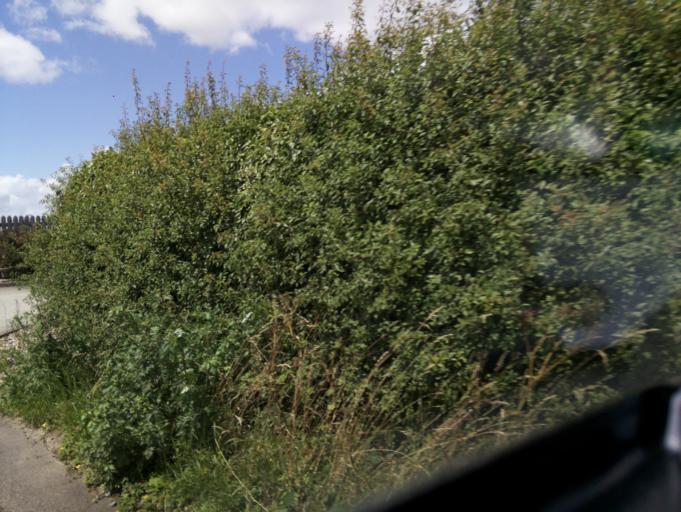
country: GB
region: England
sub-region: Nottinghamshire
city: Burton Joyce
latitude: 53.0040
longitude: -1.0745
